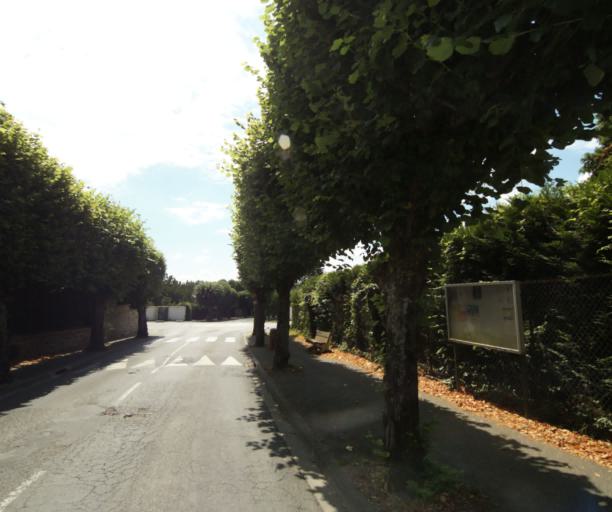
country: FR
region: Ile-de-France
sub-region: Departement de Seine-et-Marne
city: Chartrettes
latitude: 48.4862
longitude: 2.6966
